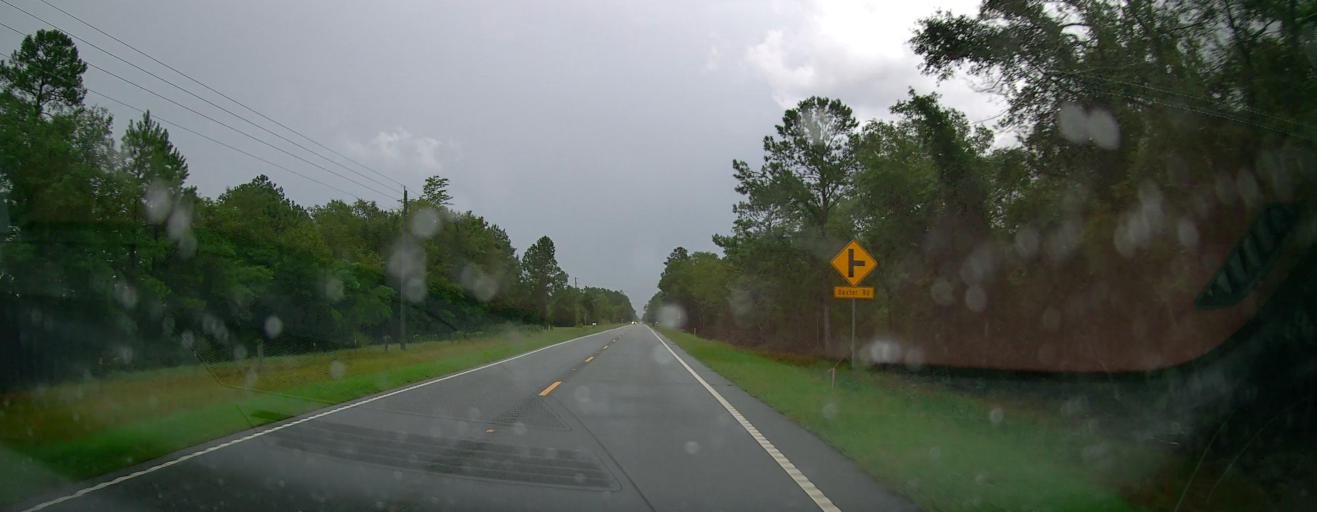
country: US
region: Georgia
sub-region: Brantley County
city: Nahunta
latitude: 31.3416
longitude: -81.9842
